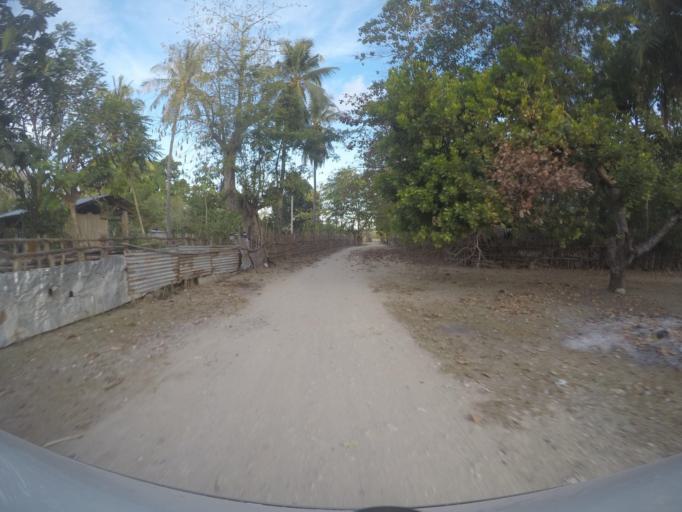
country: TL
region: Viqueque
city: Viqueque
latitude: -8.9455
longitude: 126.4491
